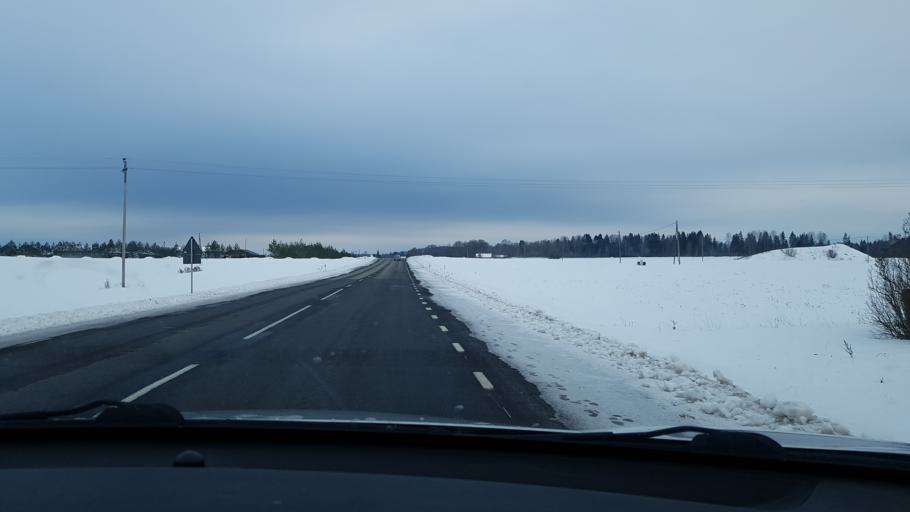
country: EE
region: Jaervamaa
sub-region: Paide linn
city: Paide
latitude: 58.8896
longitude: 25.7134
